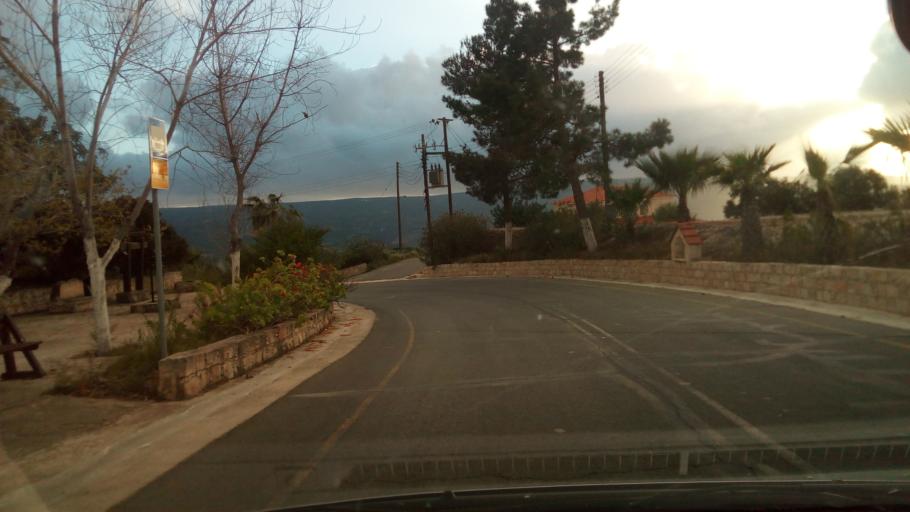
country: CY
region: Pafos
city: Polis
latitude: 34.9885
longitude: 32.4864
